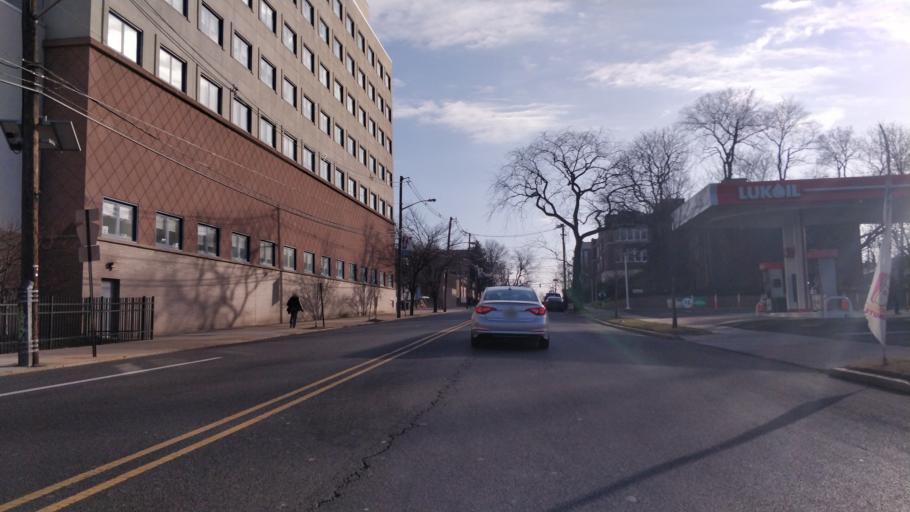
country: US
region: New Jersey
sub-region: Union County
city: Elizabeth
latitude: 40.6595
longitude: -74.2154
